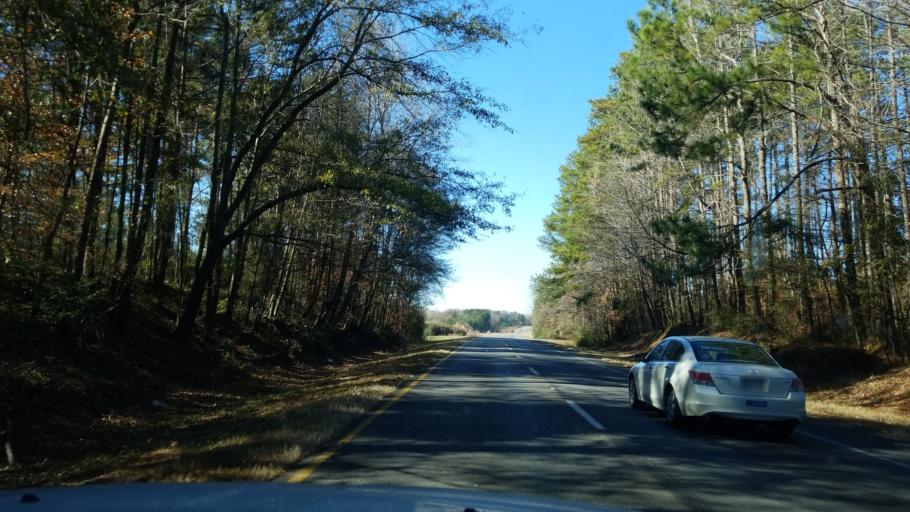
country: US
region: Alabama
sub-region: Tuscaloosa County
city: Northport
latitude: 33.2369
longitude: -87.6523
